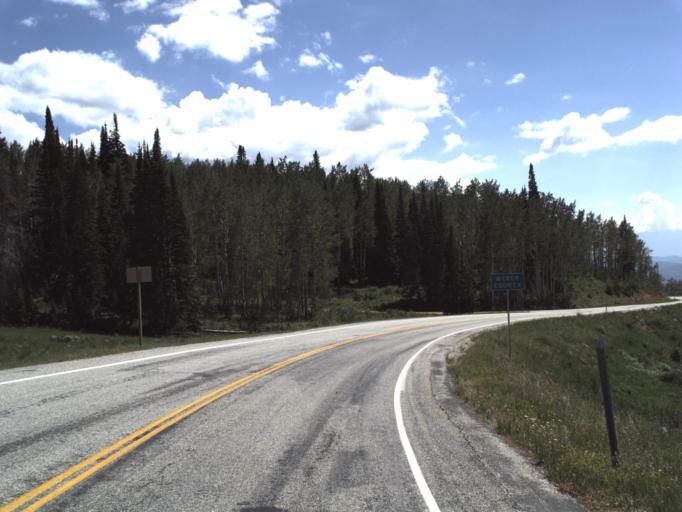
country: US
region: Utah
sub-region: Weber County
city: Wolf Creek
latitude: 41.4212
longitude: -111.5218
